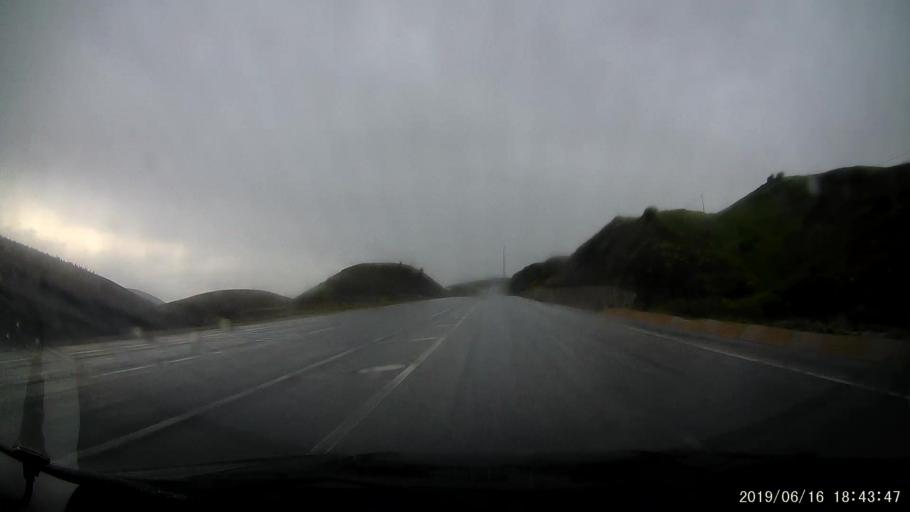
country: TR
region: Erzincan
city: Doganbeyli
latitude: 39.8716
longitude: 39.0863
